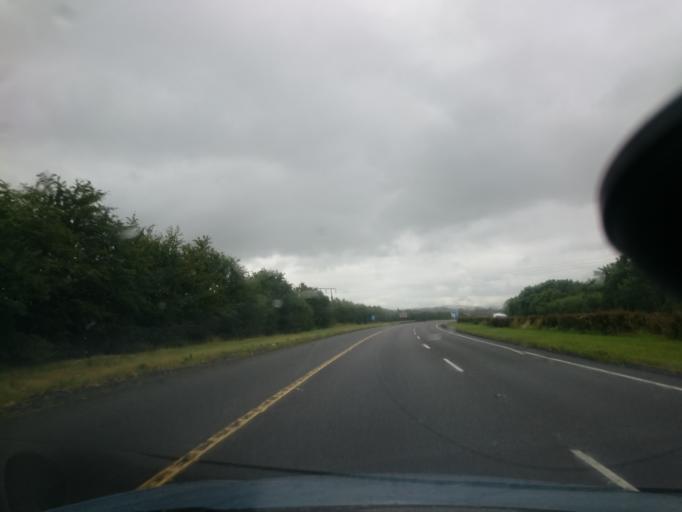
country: IE
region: Leinster
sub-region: Kildare
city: Sallins
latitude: 53.2414
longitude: -6.6515
